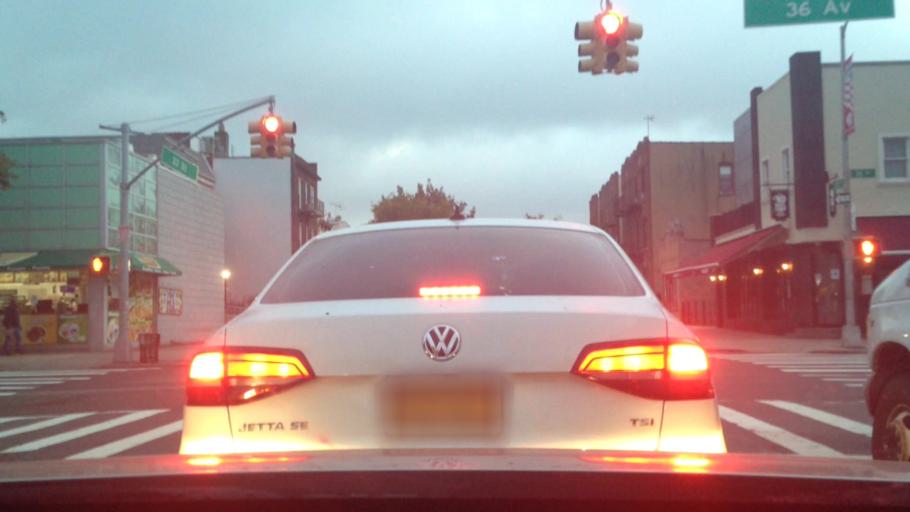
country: US
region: New York
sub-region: Queens County
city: Long Island City
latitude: 40.7557
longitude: -73.9283
